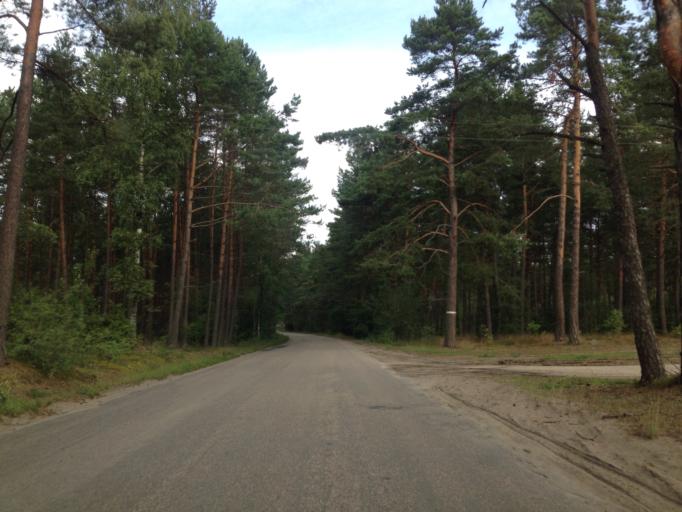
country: PL
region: Pomeranian Voivodeship
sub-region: Powiat koscierski
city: Dziemiany
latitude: 54.0203
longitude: 17.6688
